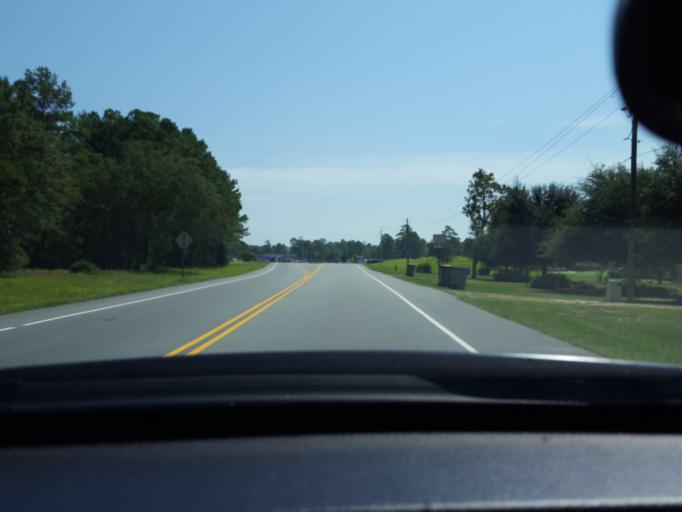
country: US
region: North Carolina
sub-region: Bladen County
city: Elizabethtown
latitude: 34.6567
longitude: -78.5035
